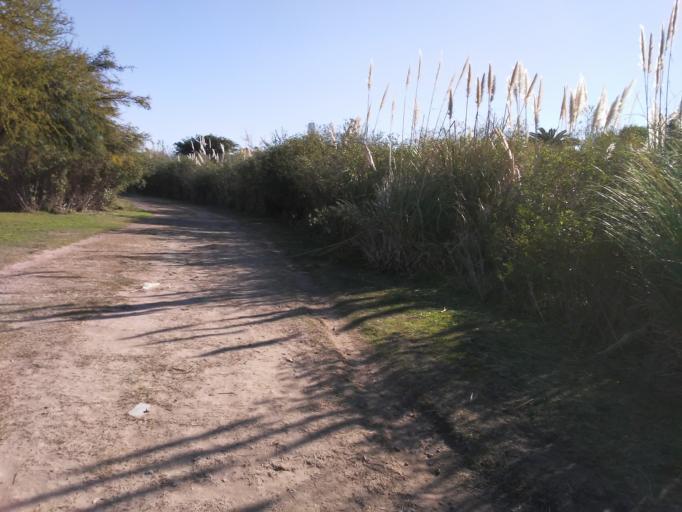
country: AR
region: Buenos Aires F.D.
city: Buenos Aires
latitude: -34.6168
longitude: -58.3418
